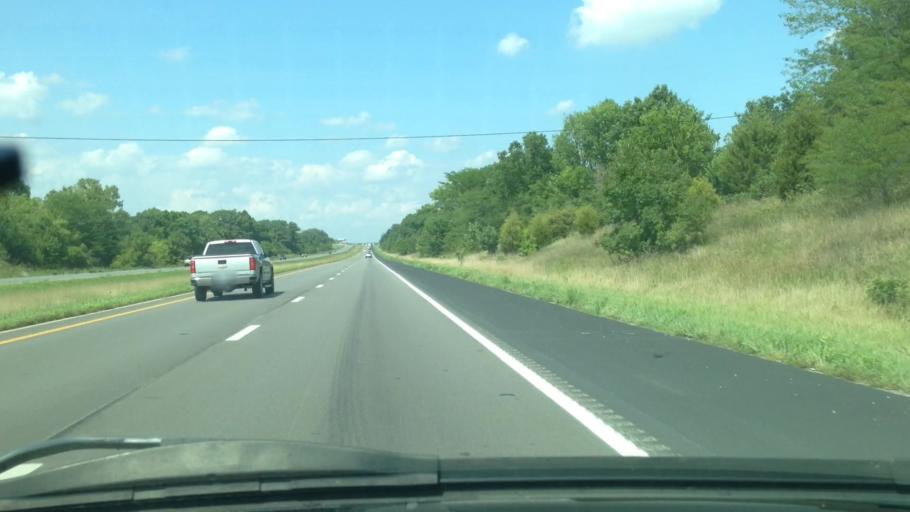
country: US
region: Missouri
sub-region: Lincoln County
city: Troy
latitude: 39.0531
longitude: -90.9738
